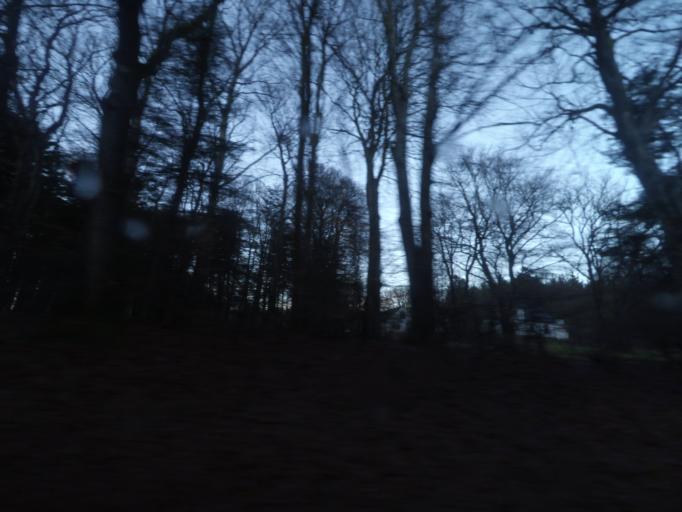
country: DK
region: Central Jutland
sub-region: Ikast-Brande Kommune
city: Brande
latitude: 56.0090
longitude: 9.0719
